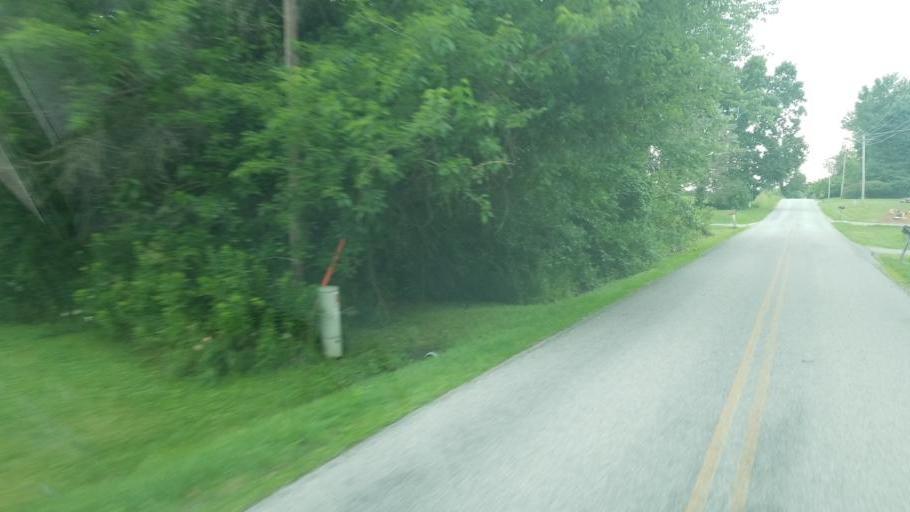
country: US
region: Ohio
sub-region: Delaware County
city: Sunbury
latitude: 40.2878
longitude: -82.8543
